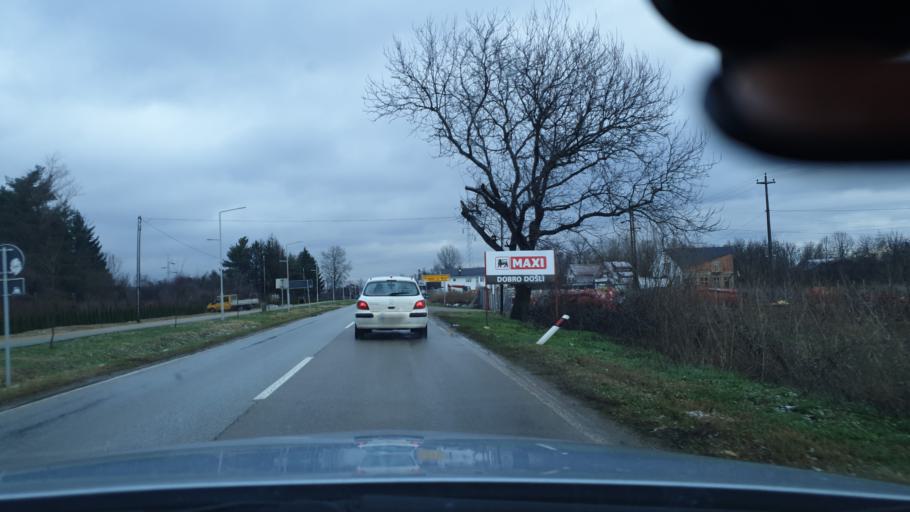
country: RS
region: Central Serbia
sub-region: Branicevski Okrug
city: Petrovac
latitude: 44.3958
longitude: 21.4043
